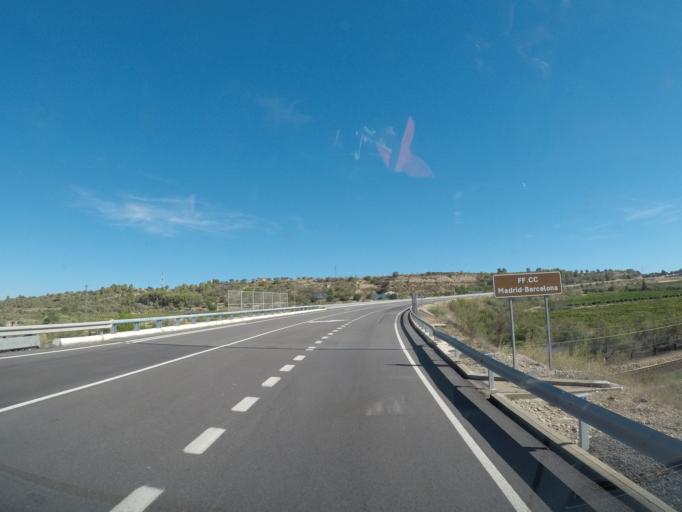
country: ES
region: Catalonia
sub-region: Provincia de Tarragona
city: Garcia
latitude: 41.1019
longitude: 0.6612
